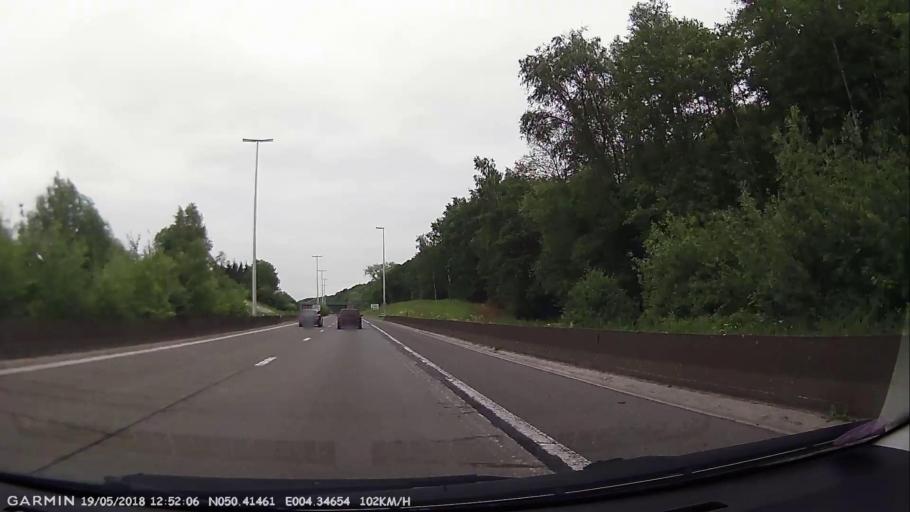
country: BE
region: Wallonia
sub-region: Province du Hainaut
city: Courcelles
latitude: 50.4150
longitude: 4.3466
